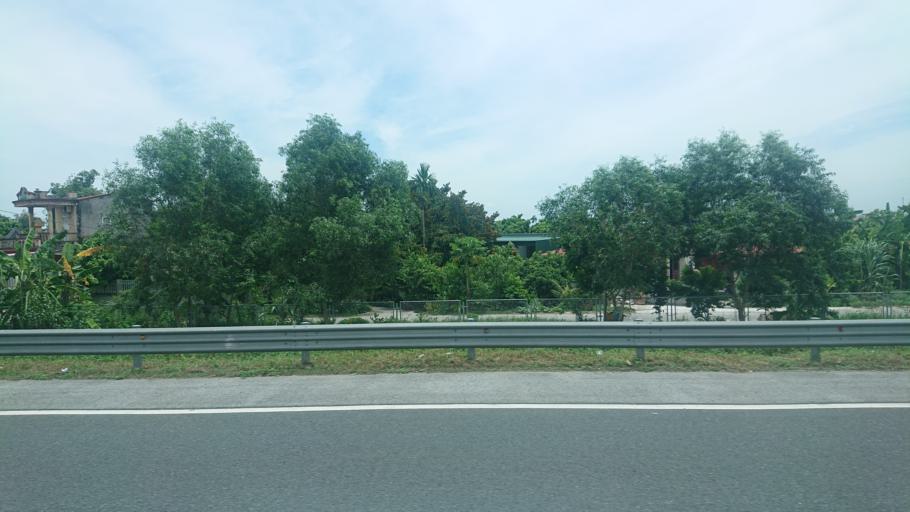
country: VN
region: Hai Phong
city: An Lao
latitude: 20.8039
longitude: 106.5232
